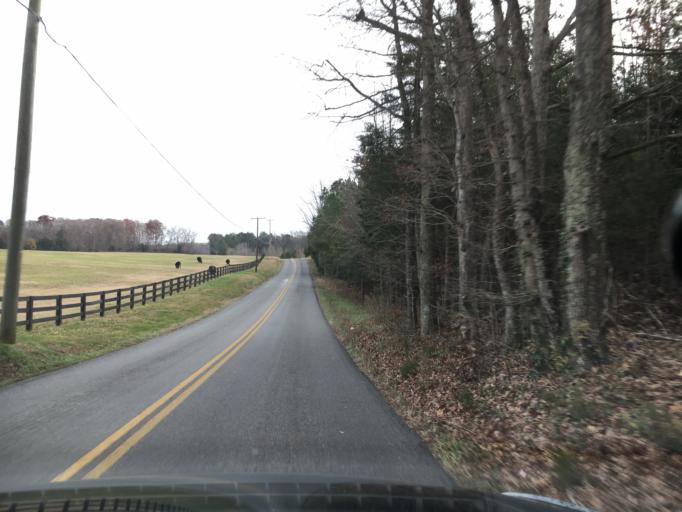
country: US
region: Virginia
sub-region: Henrico County
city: Wyndham
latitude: 37.6833
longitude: -77.6819
